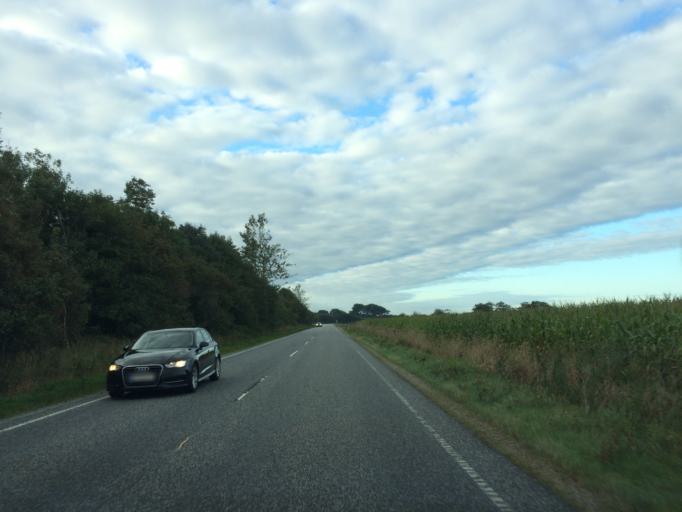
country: DK
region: Central Jutland
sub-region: Ringkobing-Skjern Kommune
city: Skjern
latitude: 55.9790
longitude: 8.5004
